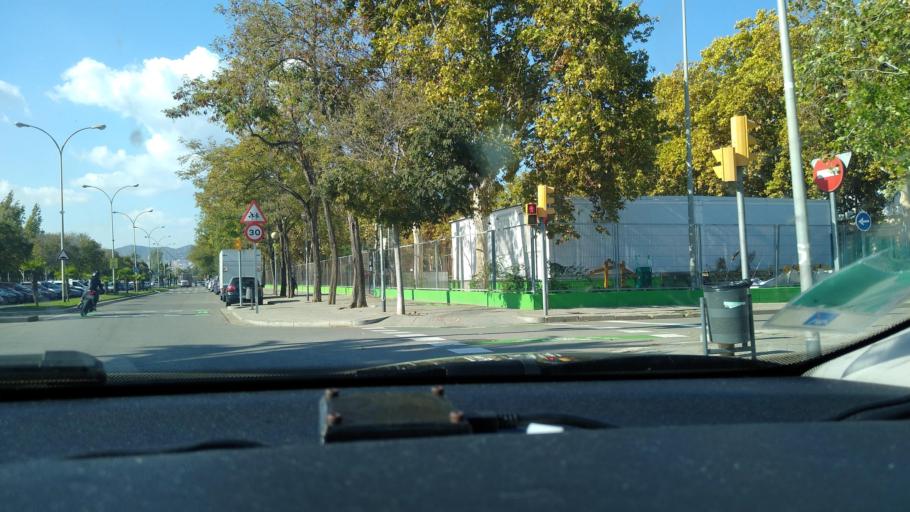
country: ES
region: Catalonia
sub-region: Provincia de Barcelona
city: Sant Adria de Besos
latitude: 41.4238
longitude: 2.2270
